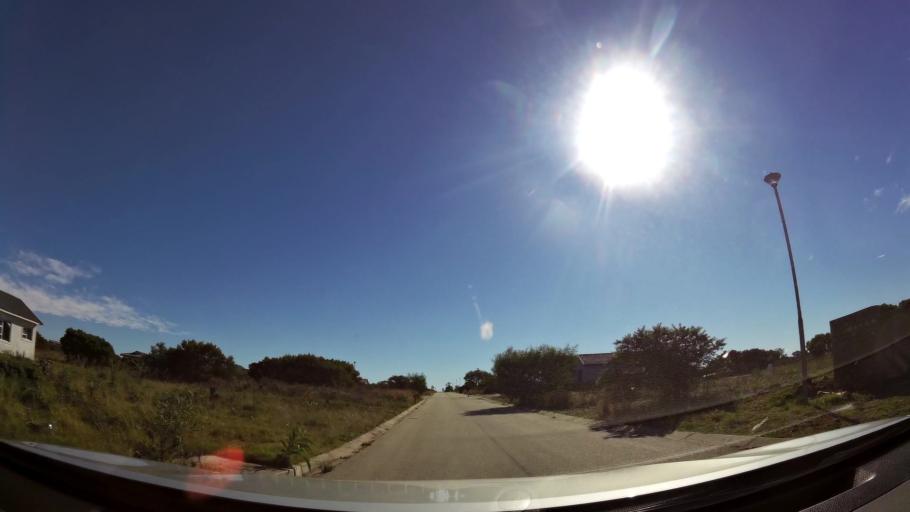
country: ZA
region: Eastern Cape
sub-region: Cacadu District Municipality
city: Jeffrey's Bay
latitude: -34.0362
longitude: 24.9082
